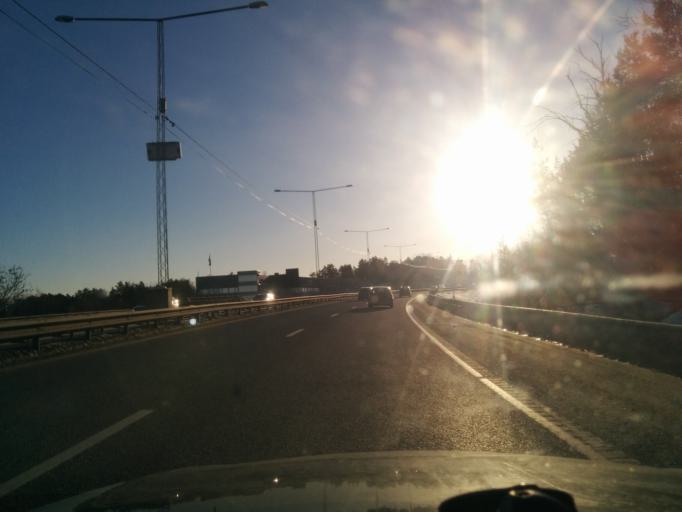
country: SE
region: Stockholm
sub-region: Taby Kommun
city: Taby
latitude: 59.4506
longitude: 18.1316
